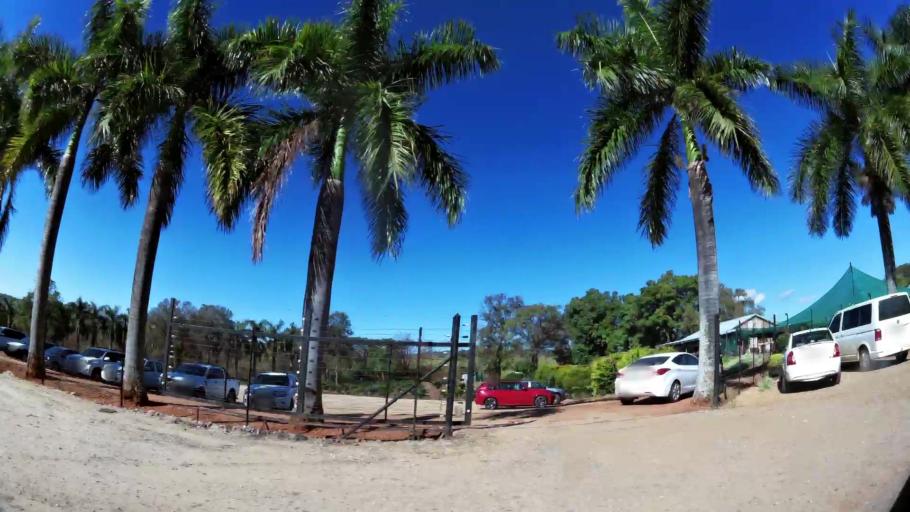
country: ZA
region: Limpopo
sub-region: Mopani District Municipality
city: Tzaneen
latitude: -23.8427
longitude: 30.1462
